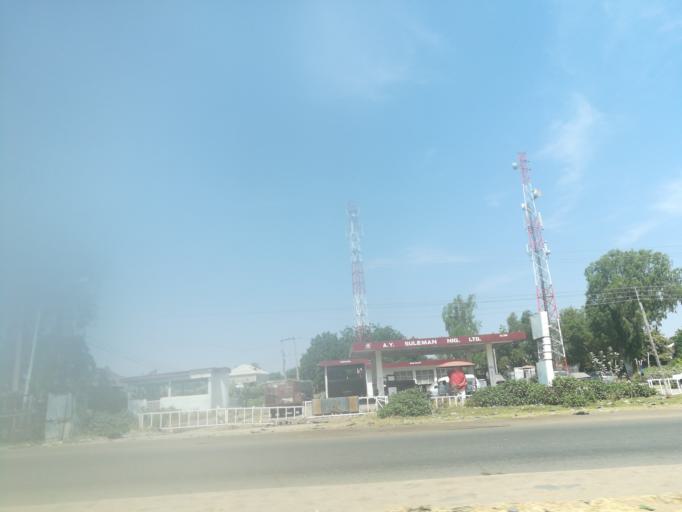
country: NG
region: Kano
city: Kano
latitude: 12.0285
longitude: 8.5172
